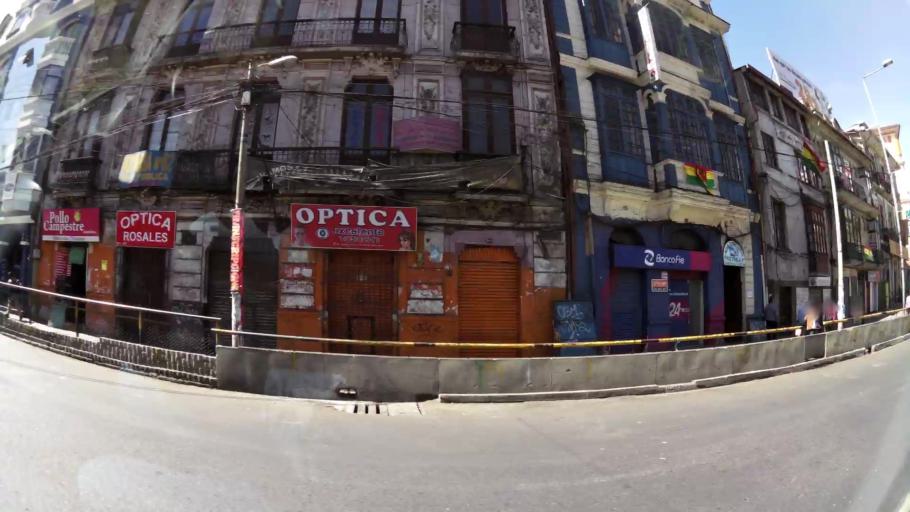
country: BO
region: La Paz
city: La Paz
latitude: -16.4939
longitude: -68.1369
